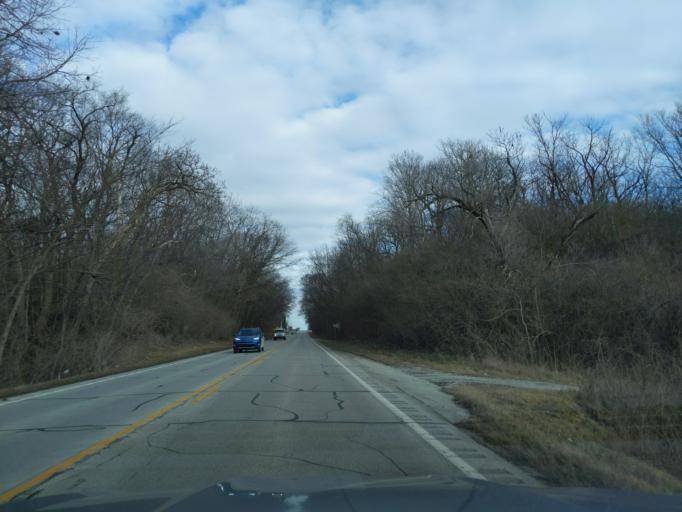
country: US
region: Indiana
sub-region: Tippecanoe County
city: Shadeland
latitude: 40.3820
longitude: -86.9320
